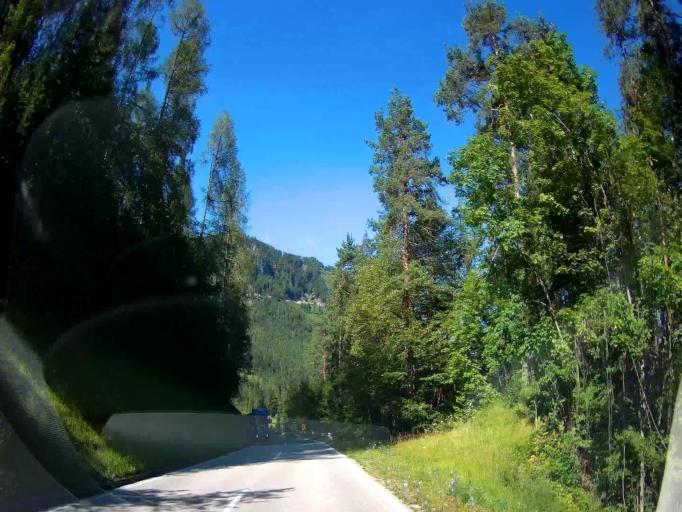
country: AT
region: Carinthia
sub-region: Politischer Bezirk Klagenfurt Land
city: Ebenthal
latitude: 46.5377
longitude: 14.4025
